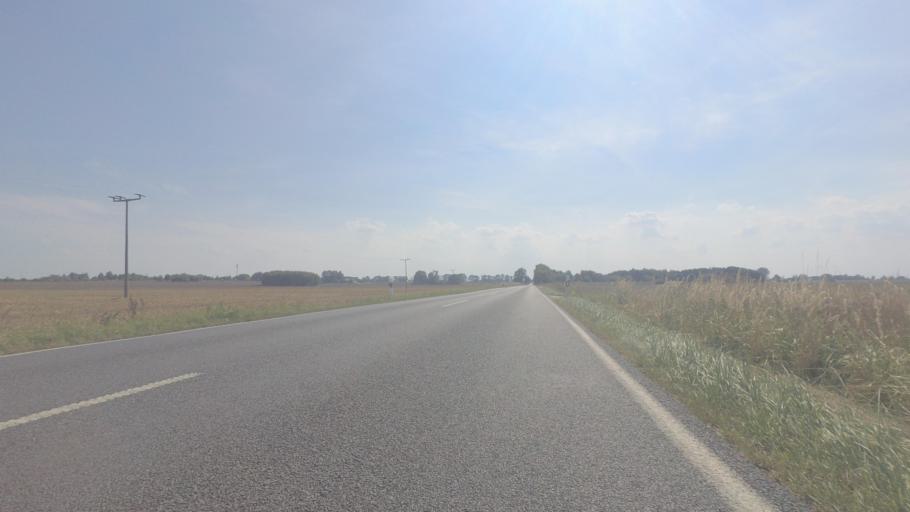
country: DE
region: Mecklenburg-Vorpommern
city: Brandshagen
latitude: 54.1583
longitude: 13.1656
